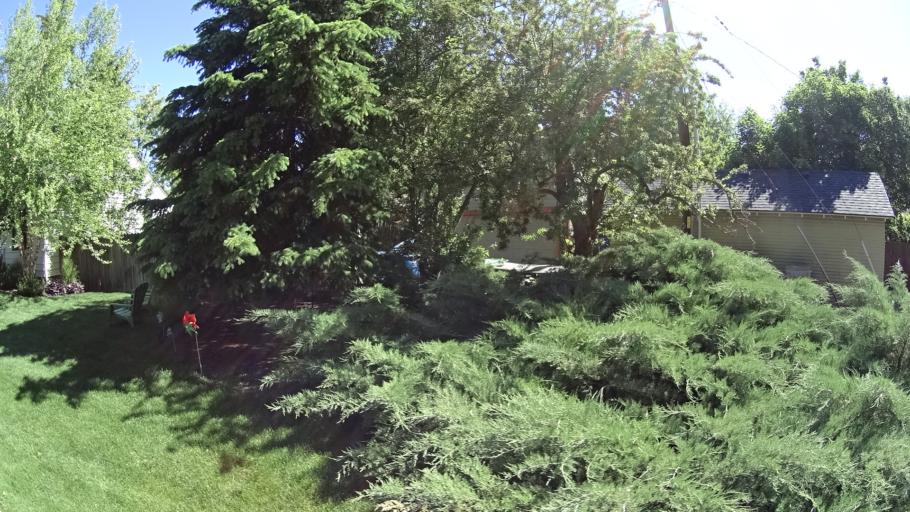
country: US
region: Idaho
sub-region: Ada County
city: Garden City
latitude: 43.6316
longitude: -116.2206
